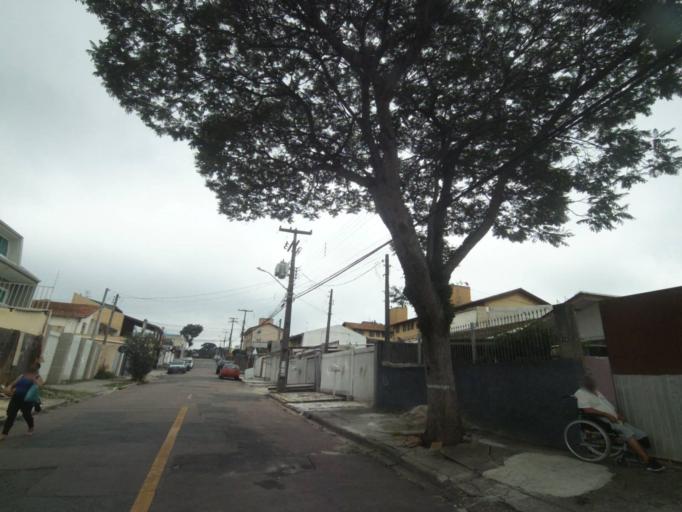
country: BR
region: Parana
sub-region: Curitiba
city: Curitiba
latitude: -25.4854
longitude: -49.3508
